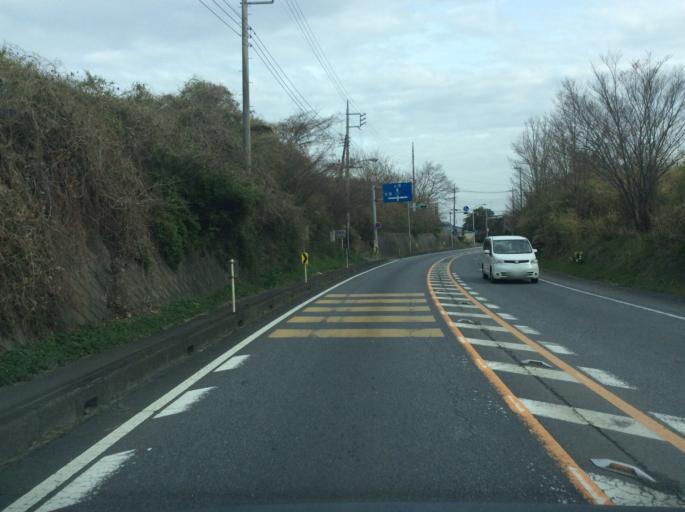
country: JP
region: Ibaraki
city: Tsukuba
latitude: 36.1530
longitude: 140.1162
